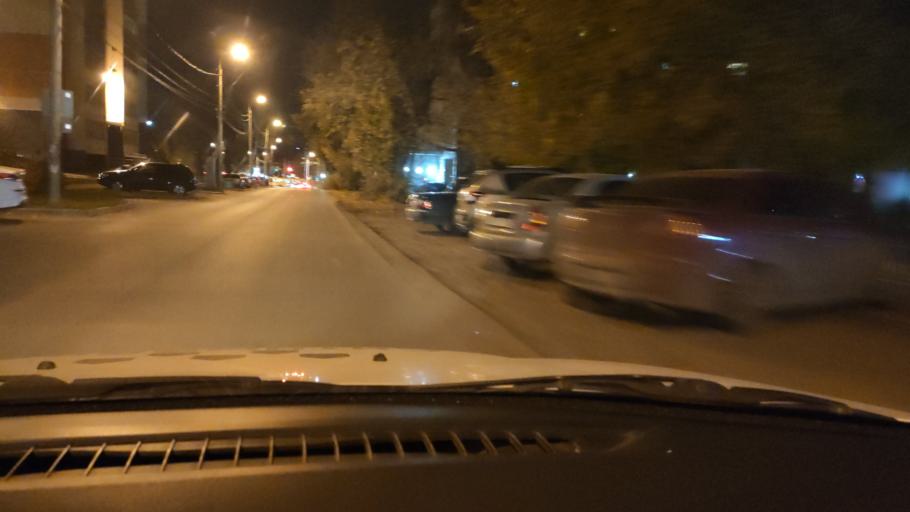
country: RU
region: Perm
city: Perm
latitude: 57.9950
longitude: 56.2209
